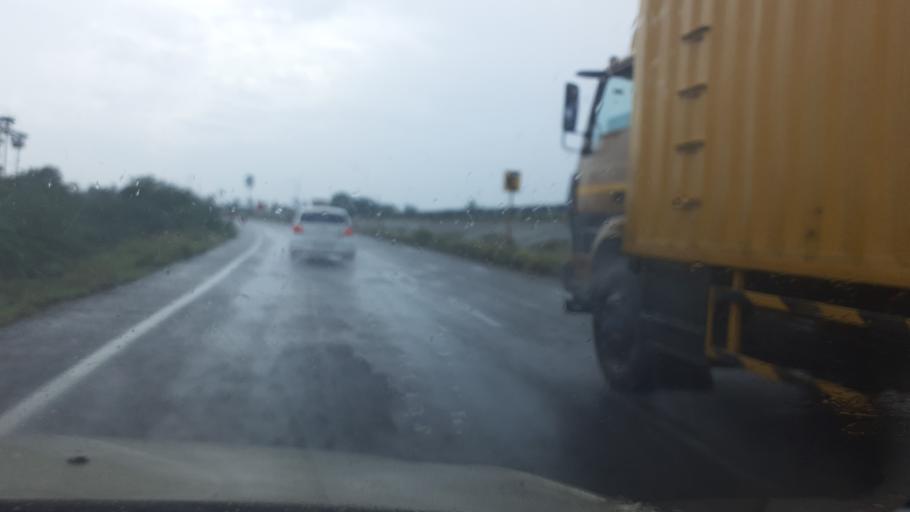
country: IN
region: Tamil Nadu
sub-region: Thoothukkudi
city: Kayattar
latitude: 8.9266
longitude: 77.7668
